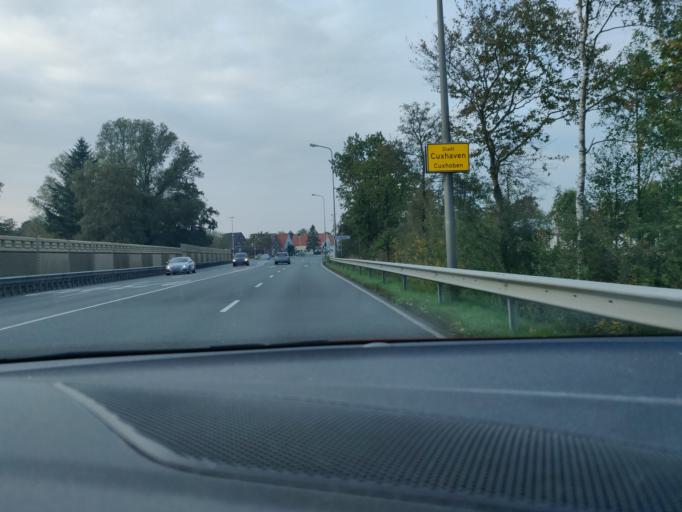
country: DE
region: Lower Saxony
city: Cuxhaven
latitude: 53.8439
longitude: 8.7316
